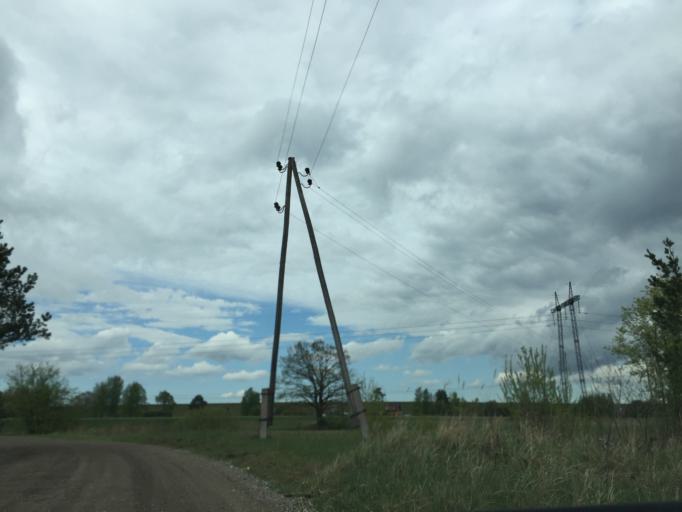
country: LV
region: Kekava
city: Kekava
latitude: 56.8171
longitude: 24.2933
